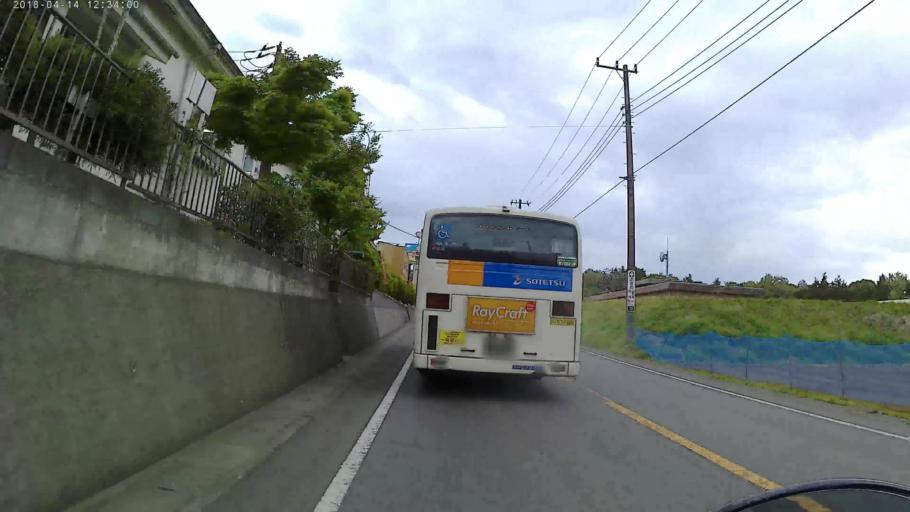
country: JP
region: Kanagawa
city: Atsugi
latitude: 35.4293
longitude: 139.4100
